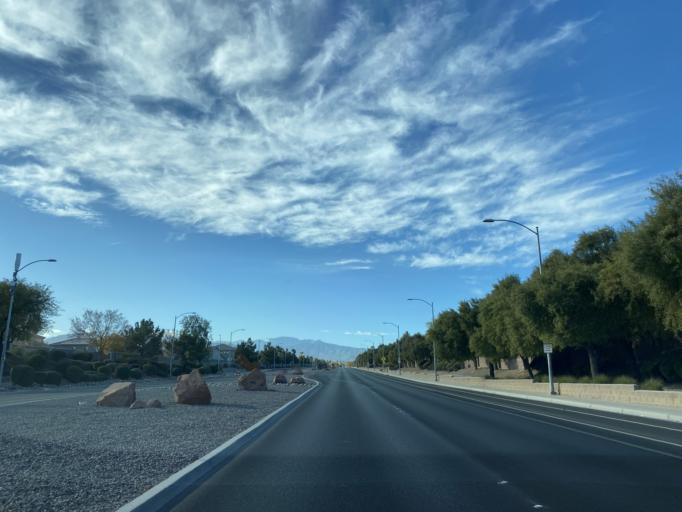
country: US
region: Nevada
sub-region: Clark County
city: North Las Vegas
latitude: 36.3054
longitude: -115.2632
